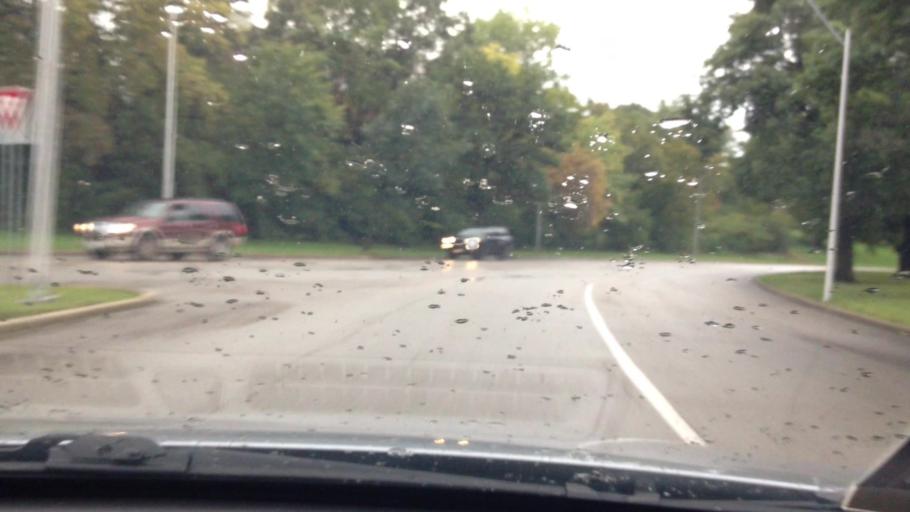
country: US
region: Kansas
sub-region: Johnson County
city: Mission Hills
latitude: 39.0124
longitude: -94.5706
